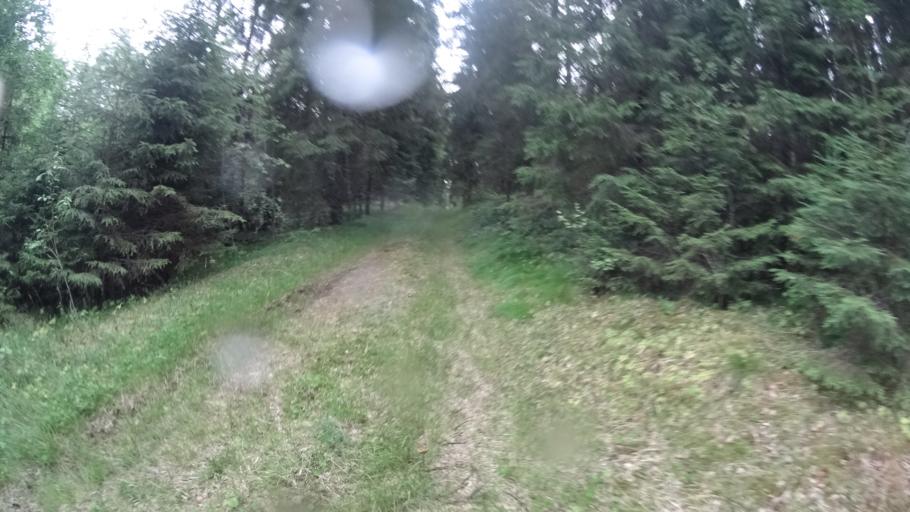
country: FI
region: Uusimaa
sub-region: Helsinki
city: Karkkila
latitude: 60.5943
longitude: 24.1703
